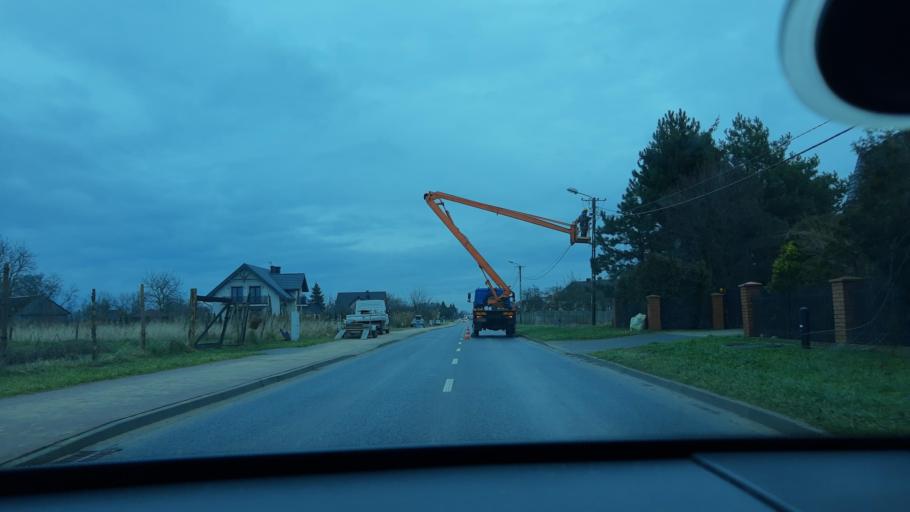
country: PL
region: Lodz Voivodeship
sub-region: Powiat sieradzki
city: Sieradz
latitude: 51.5891
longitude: 18.6963
